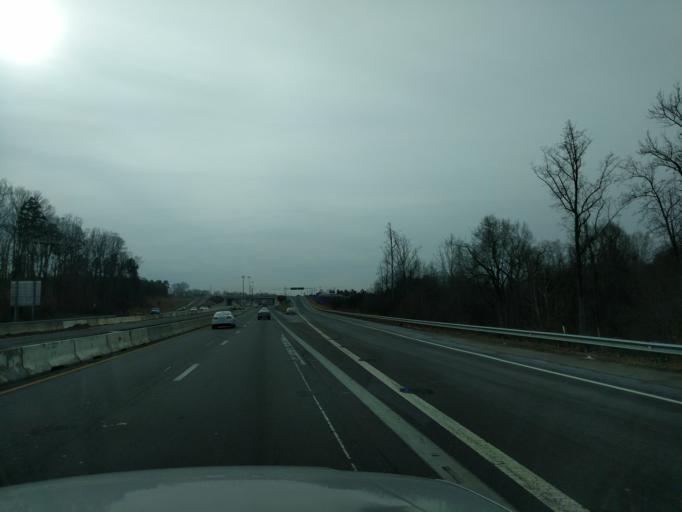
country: US
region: North Carolina
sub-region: Iredell County
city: Mooresville
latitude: 35.5846
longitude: -80.8577
